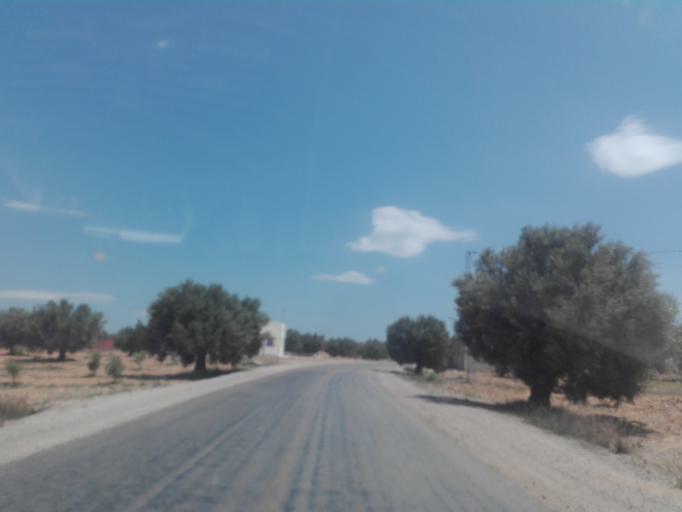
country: TN
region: Safaqis
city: Sfax
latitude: 34.6227
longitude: 10.6096
